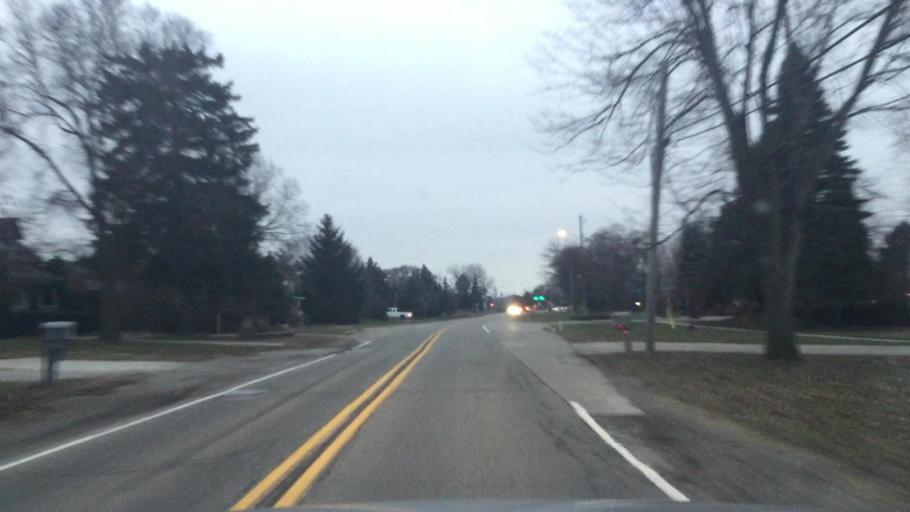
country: US
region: Michigan
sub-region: Macomb County
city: Fraser
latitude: 42.5822
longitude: -82.9744
